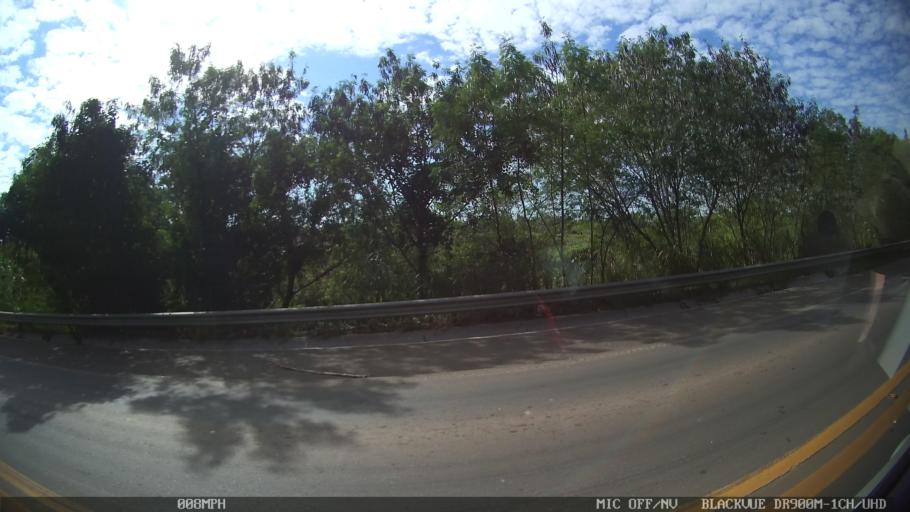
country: BR
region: Sao Paulo
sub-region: Santa Barbara D'Oeste
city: Santa Barbara d'Oeste
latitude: -22.7058
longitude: -47.4529
